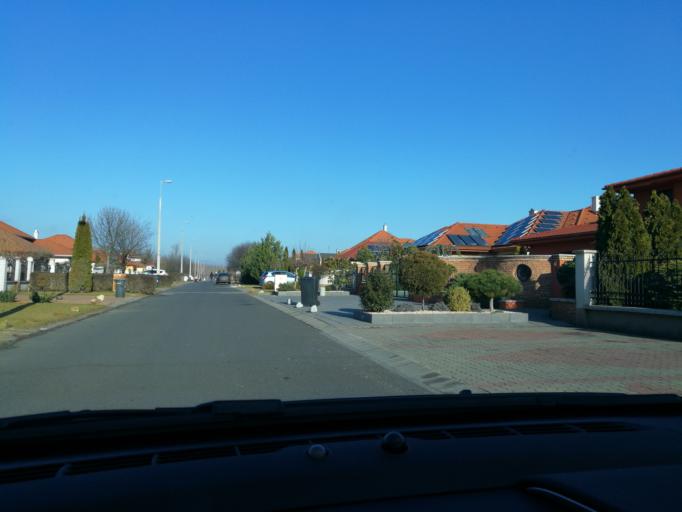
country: HU
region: Szabolcs-Szatmar-Bereg
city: Nyiregyhaza
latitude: 47.9736
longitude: 21.7326
